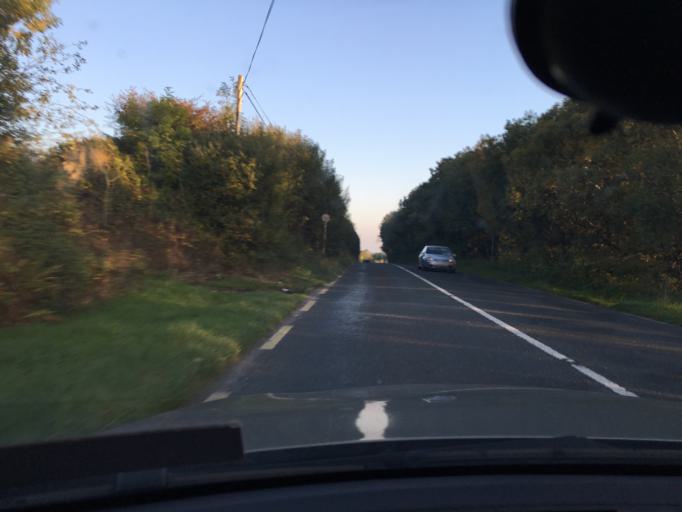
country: IE
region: Connaught
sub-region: County Galway
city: Moycullen
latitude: 53.3649
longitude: -9.2218
